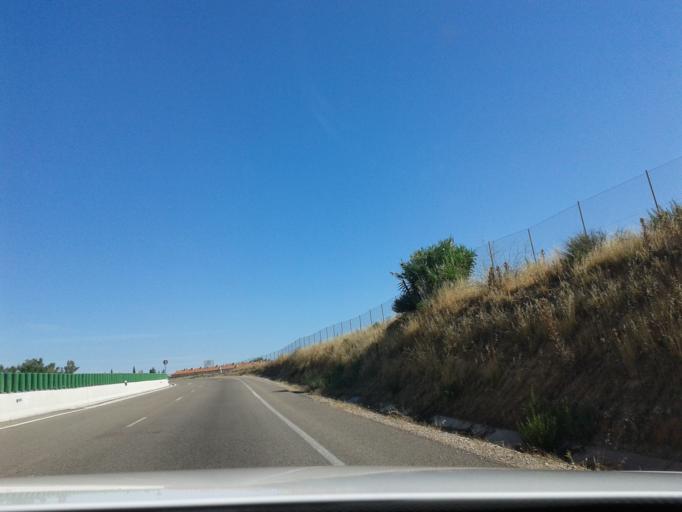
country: ES
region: Castille-La Mancha
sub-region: Provincia de Guadalajara
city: Azuqueca de Henares
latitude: 40.5753
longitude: -3.2540
